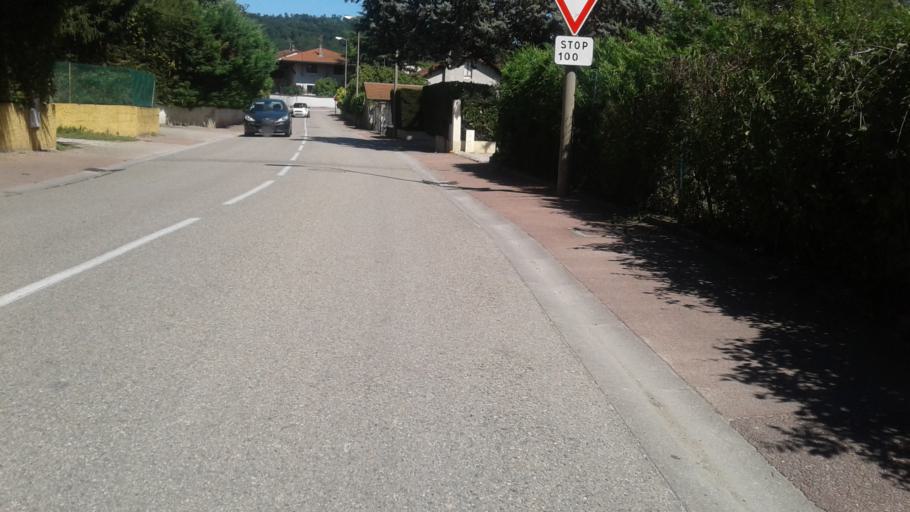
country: FR
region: Rhone-Alpes
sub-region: Departement de l'Ain
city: La Boisse
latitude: 45.8390
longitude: 5.0297
